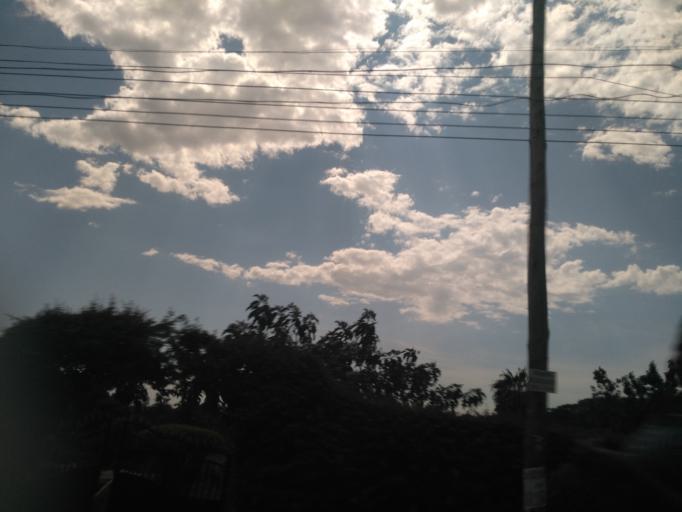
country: TZ
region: Mwanza
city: Mwanza
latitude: -2.5101
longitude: 32.9093
